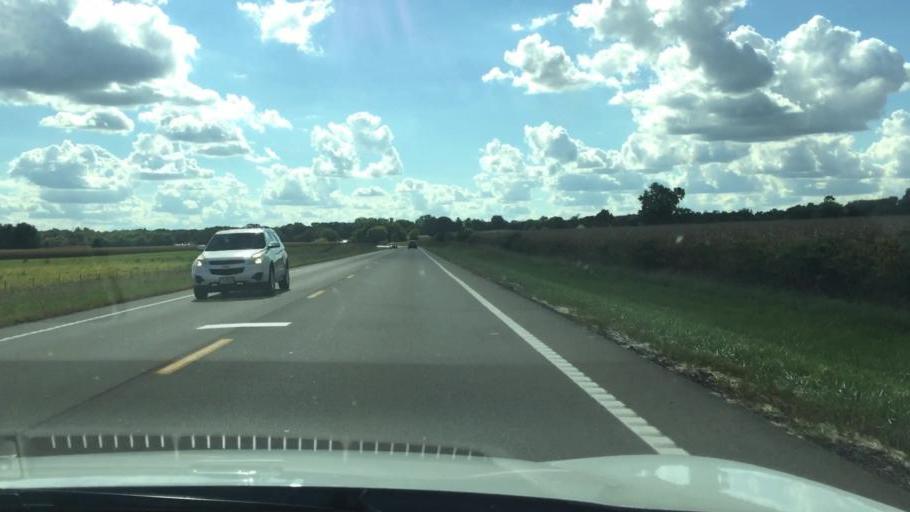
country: US
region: Ohio
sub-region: Clark County
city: Northridge
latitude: 40.0046
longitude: -83.7162
